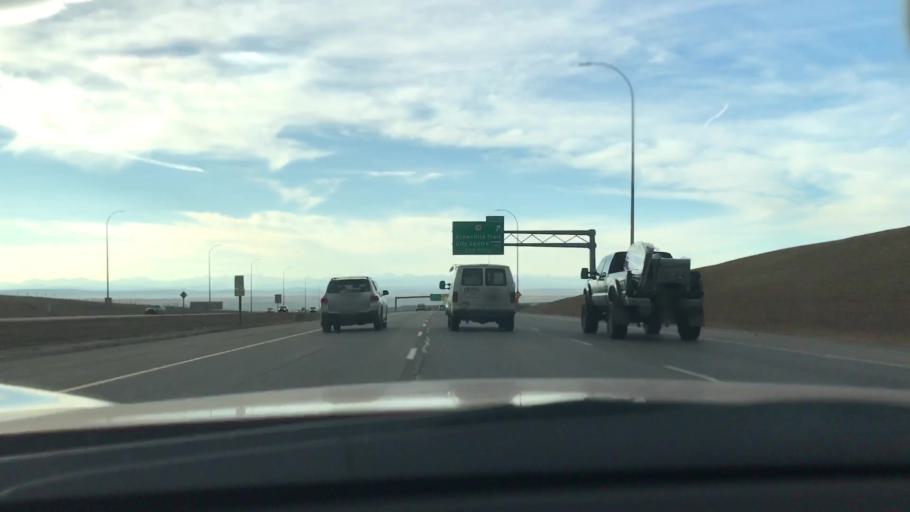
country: CA
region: Alberta
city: Calgary
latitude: 51.1387
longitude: -114.2128
